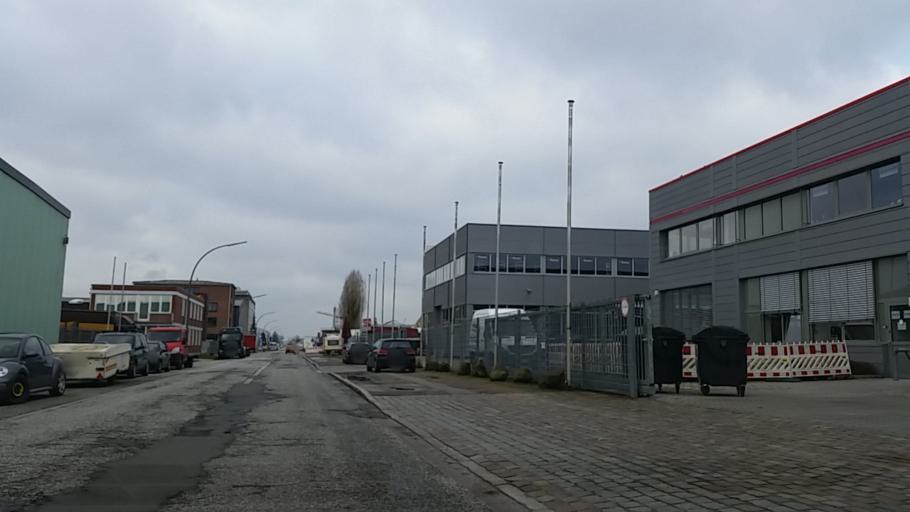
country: DE
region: Hamburg
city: Wandsbek
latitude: 53.5279
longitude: 10.1044
